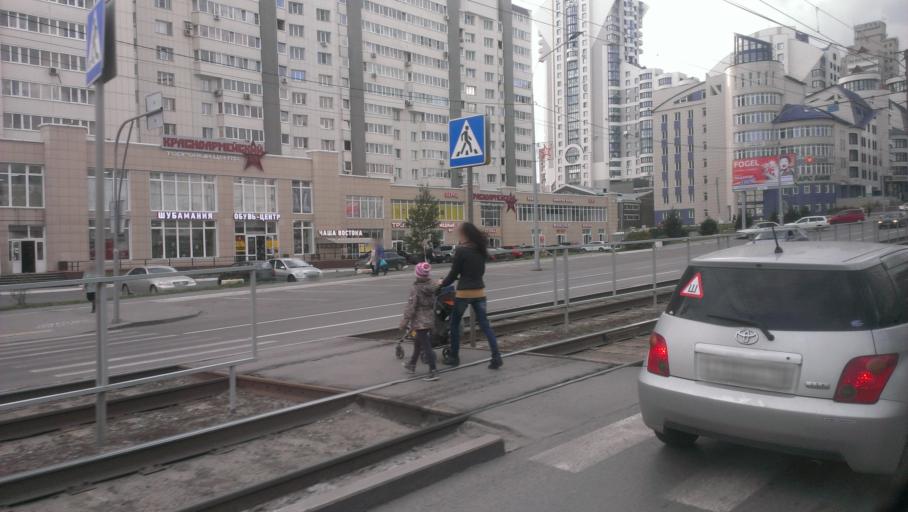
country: RU
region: Altai Krai
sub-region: Gorod Barnaulskiy
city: Barnaul
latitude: 53.3392
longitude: 83.7728
